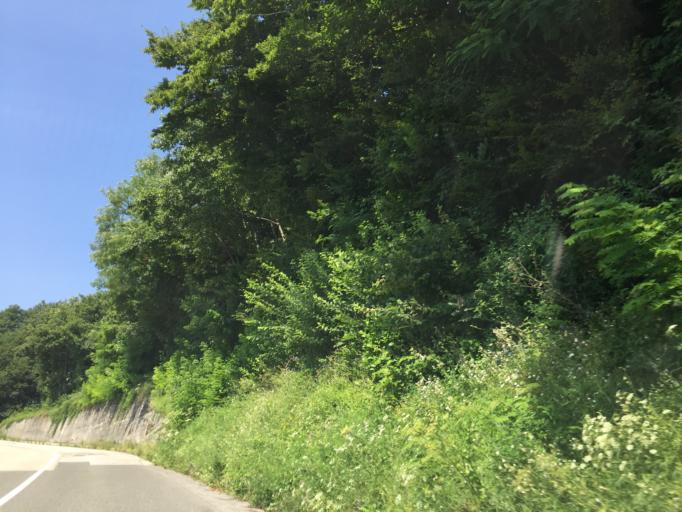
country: SI
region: Trbovlje
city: Trbovlje
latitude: 46.1826
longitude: 15.0521
